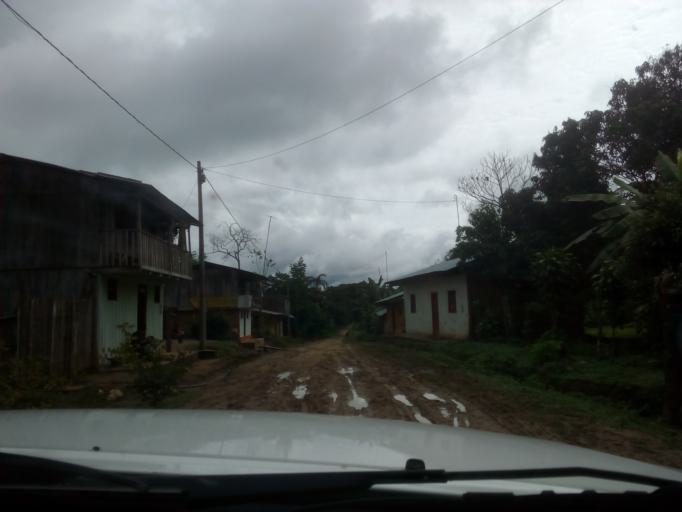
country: PE
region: San Martin
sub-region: Provincia de Lamas
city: Lamas
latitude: -6.4111
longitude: -76.4635
